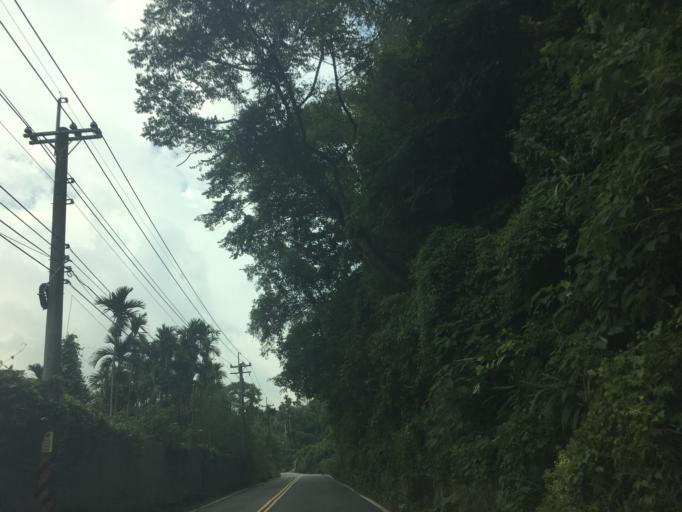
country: TW
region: Taiwan
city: Fengyuan
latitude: 24.3328
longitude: 120.9205
